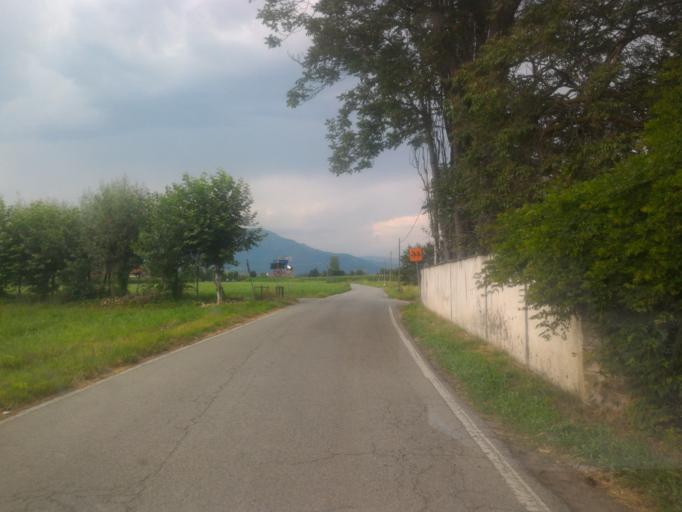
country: IT
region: Piedmont
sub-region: Provincia di Torino
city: Riva
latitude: 44.8868
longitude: 7.3994
